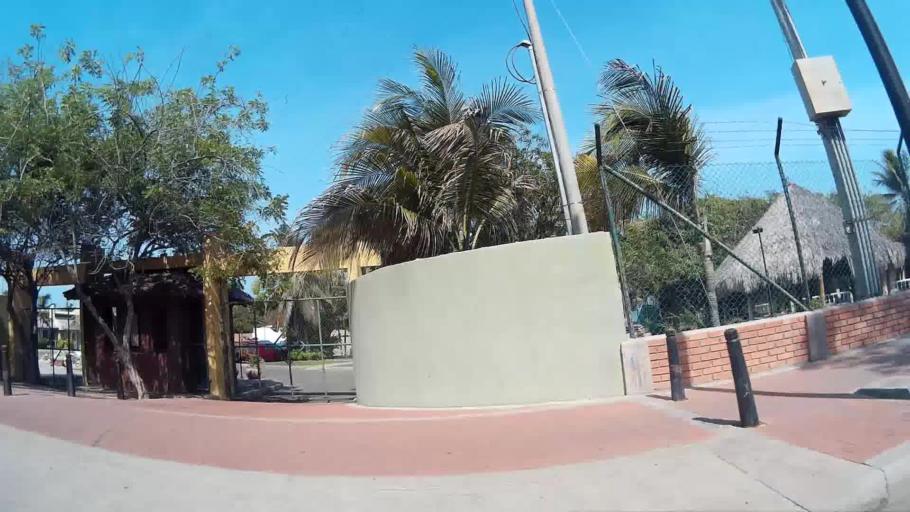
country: CO
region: Magdalena
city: Santa Marta
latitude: 11.1268
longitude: -74.2316
